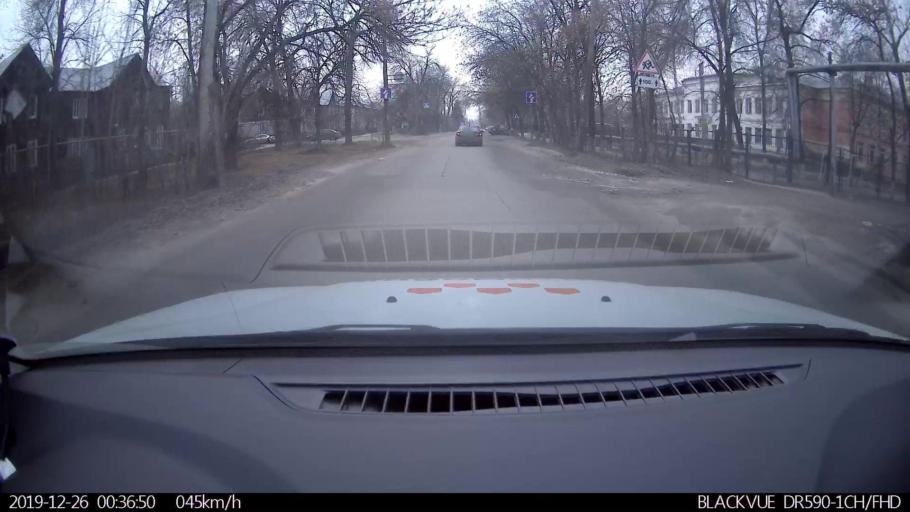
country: RU
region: Nizjnij Novgorod
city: Nizhniy Novgorod
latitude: 56.2911
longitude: 43.9057
